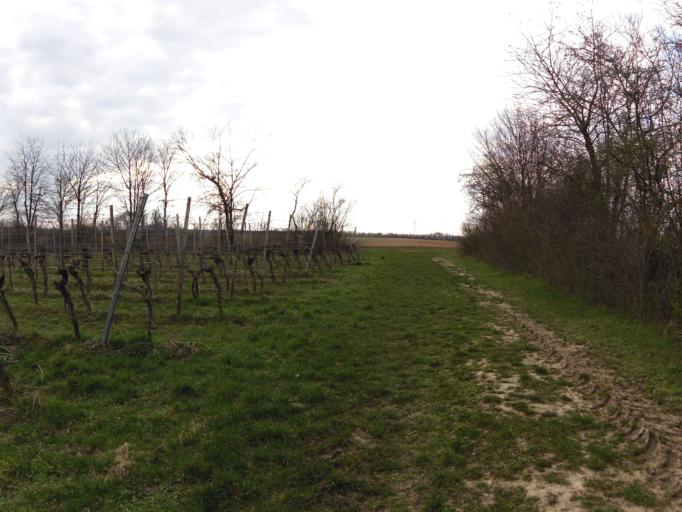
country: DE
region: Bavaria
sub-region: Regierungsbezirk Unterfranken
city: Buchbrunn
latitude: 49.7396
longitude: 10.1172
